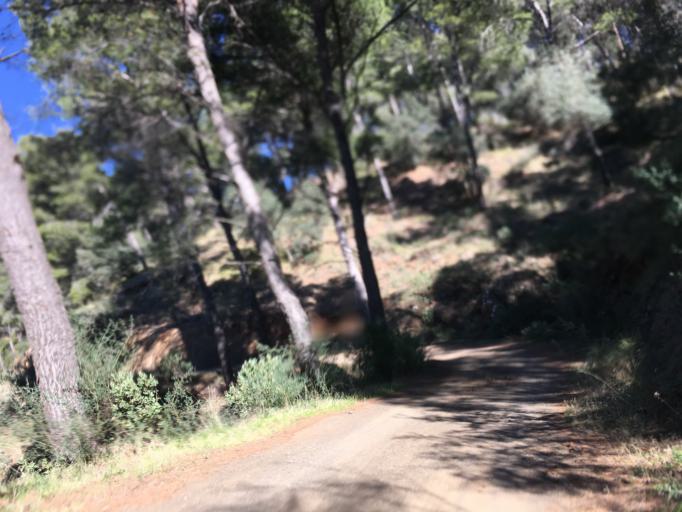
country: ES
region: Andalusia
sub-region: Provincia de Malaga
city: Malaga
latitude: 36.8026
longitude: -4.3994
